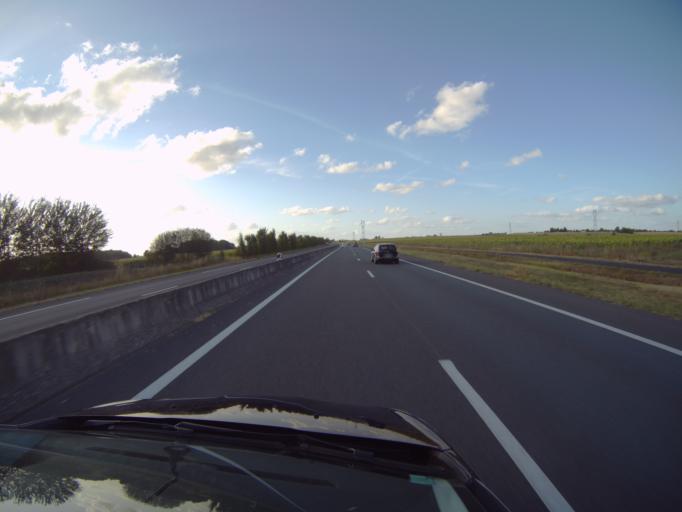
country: FR
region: Pays de la Loire
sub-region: Departement de Maine-et-Loire
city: Doue-la-Fontaine
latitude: 47.2230
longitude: -0.3073
